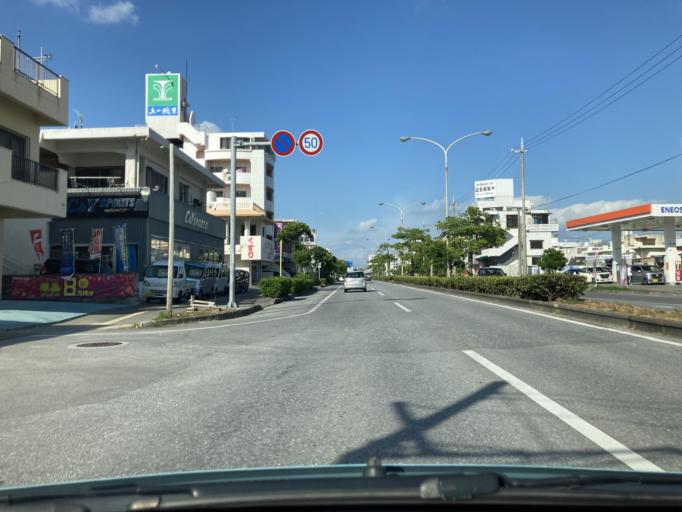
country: JP
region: Okinawa
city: Okinawa
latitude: 26.3139
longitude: 127.8293
